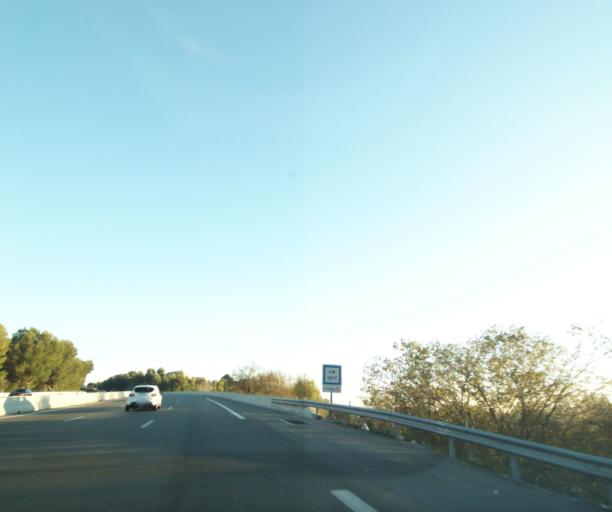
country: FR
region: Provence-Alpes-Cote d'Azur
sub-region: Departement des Bouches-du-Rhone
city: Ceyreste
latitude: 43.2021
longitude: 5.6331
